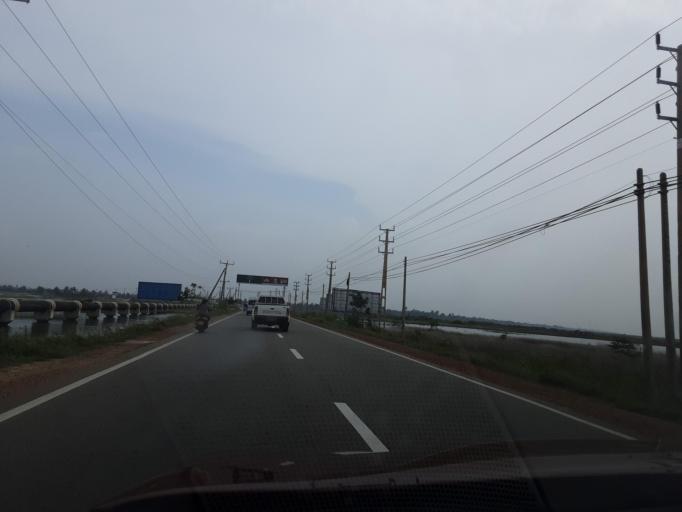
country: LK
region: Northern Province
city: Jaffna
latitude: 9.6631
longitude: 80.0660
